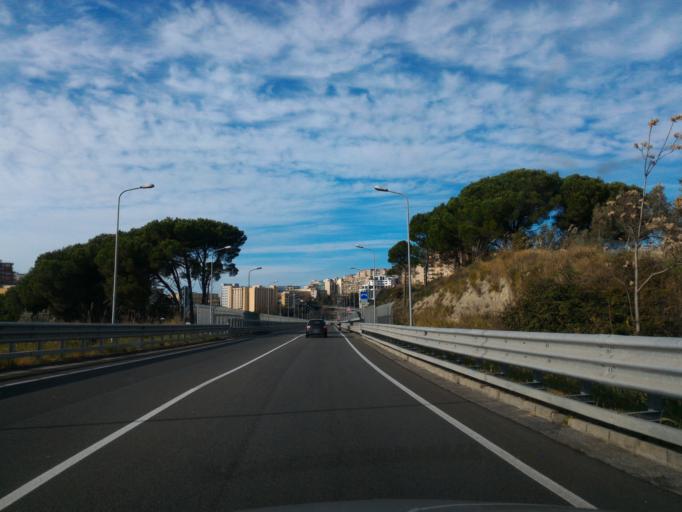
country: IT
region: Calabria
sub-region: Provincia di Catanzaro
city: Siano
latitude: 38.9111
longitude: 16.5977
